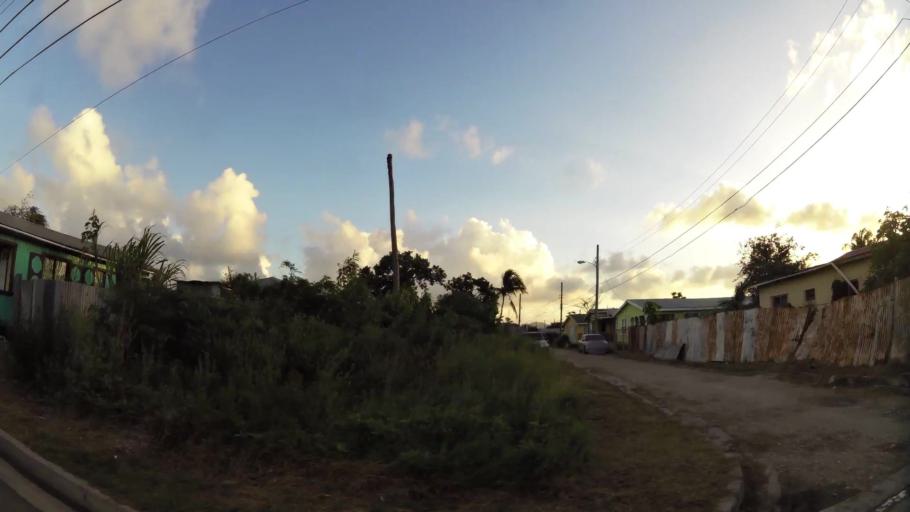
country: AG
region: Saint John
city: Saint John's
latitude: 17.1330
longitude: -61.8408
